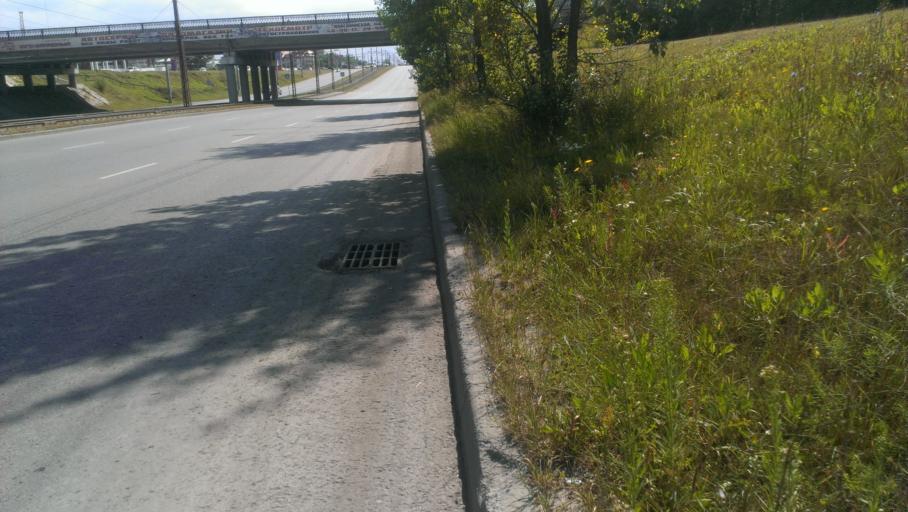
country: RU
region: Altai Krai
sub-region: Gorod Barnaulskiy
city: Barnaul
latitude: 53.3415
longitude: 83.6952
